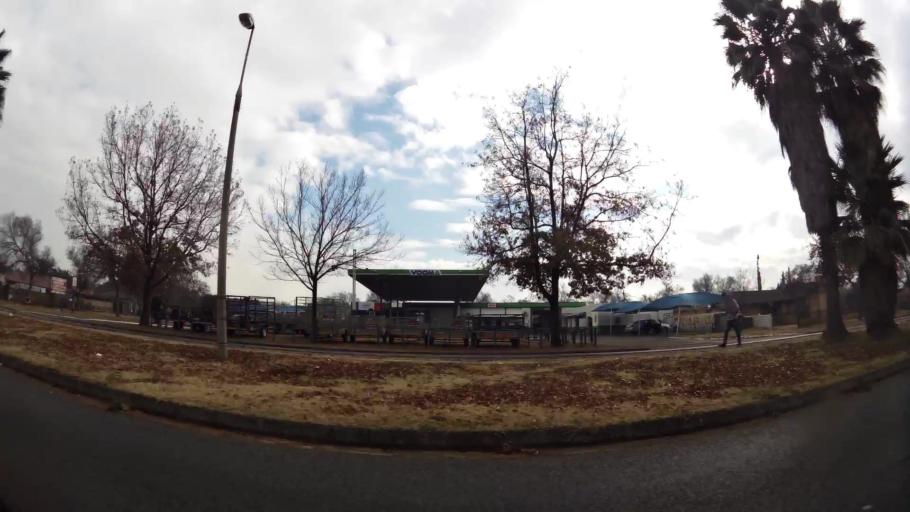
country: ZA
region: Gauteng
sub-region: Sedibeng District Municipality
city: Vanderbijlpark
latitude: -26.6971
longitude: 27.8438
